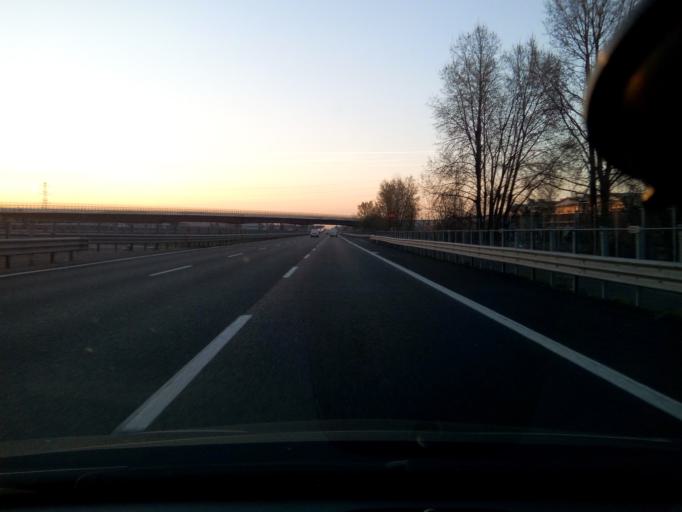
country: IT
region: Lombardy
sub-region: Citta metropolitana di Milano
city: Lainate
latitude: 45.5762
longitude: 9.0075
